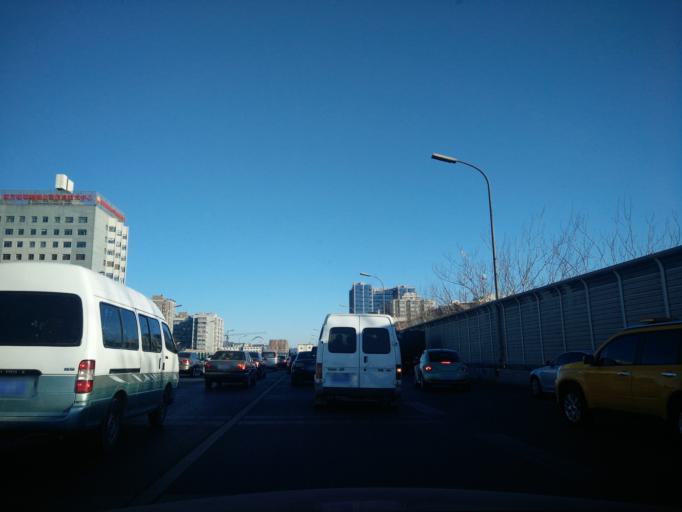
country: CN
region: Beijing
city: Lugu
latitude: 39.8966
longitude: 116.2052
